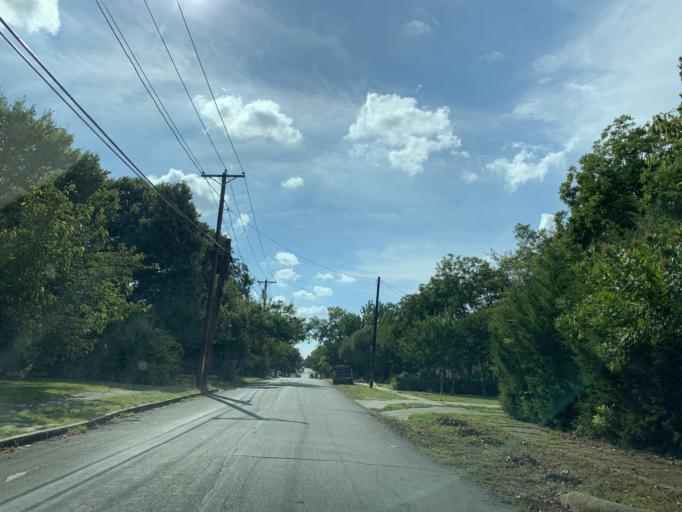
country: US
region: Texas
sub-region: Dallas County
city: Cockrell Hill
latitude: 32.7338
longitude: -96.8413
